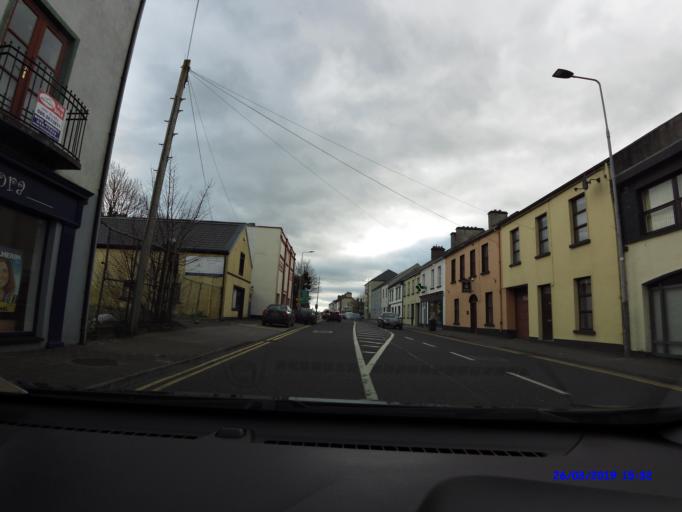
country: IE
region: Connaught
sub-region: Maigh Eo
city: Ballina
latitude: 54.1138
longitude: -9.1586
